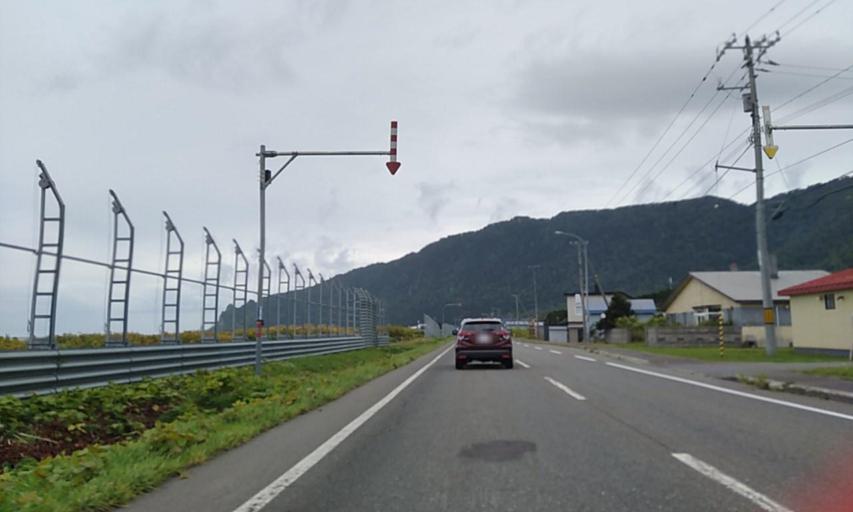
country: JP
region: Hokkaido
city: Makubetsu
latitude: 45.0715
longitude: 142.4683
